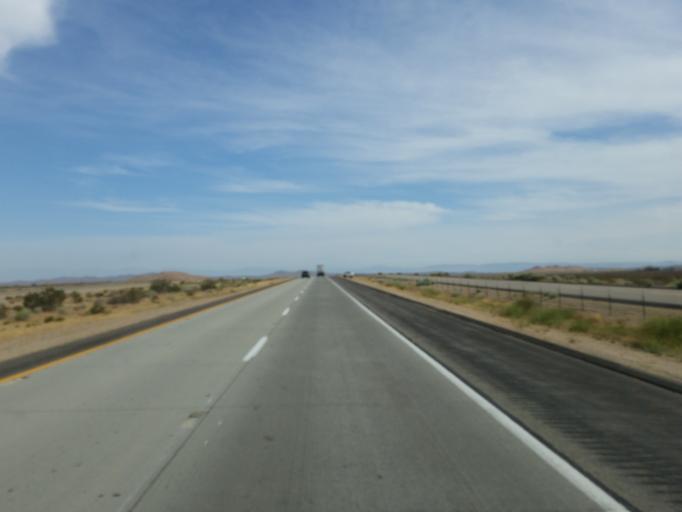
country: US
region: California
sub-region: Kern County
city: Mojave
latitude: 35.0541
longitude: -118.1133
